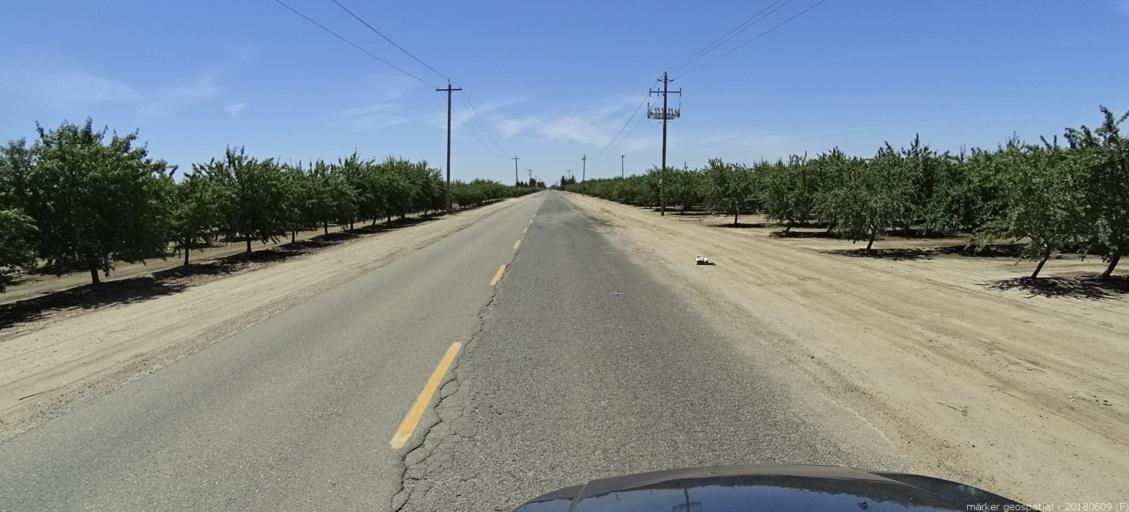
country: US
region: California
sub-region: Madera County
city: Parkwood
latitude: 36.9324
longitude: -120.0652
